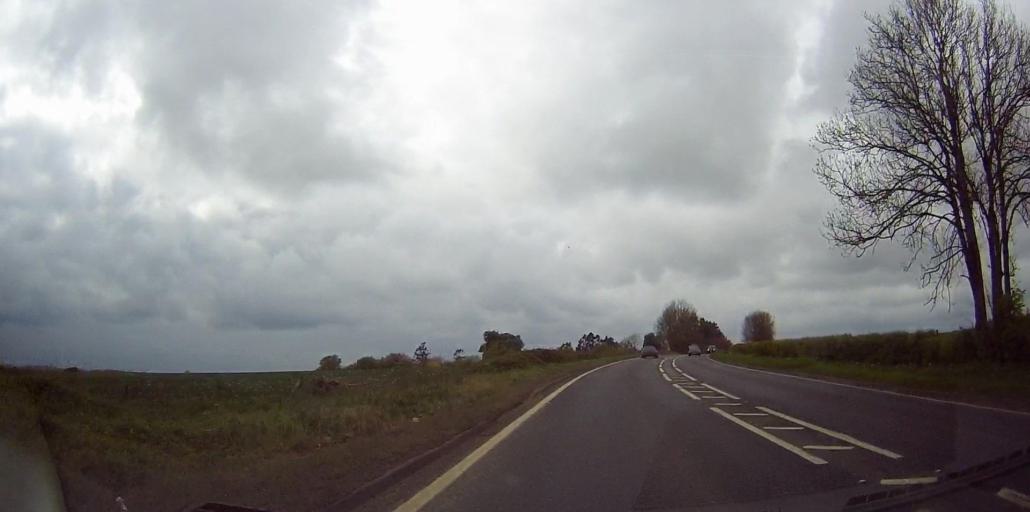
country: GB
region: England
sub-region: Kent
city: Lenham
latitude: 51.2270
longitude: 0.7589
